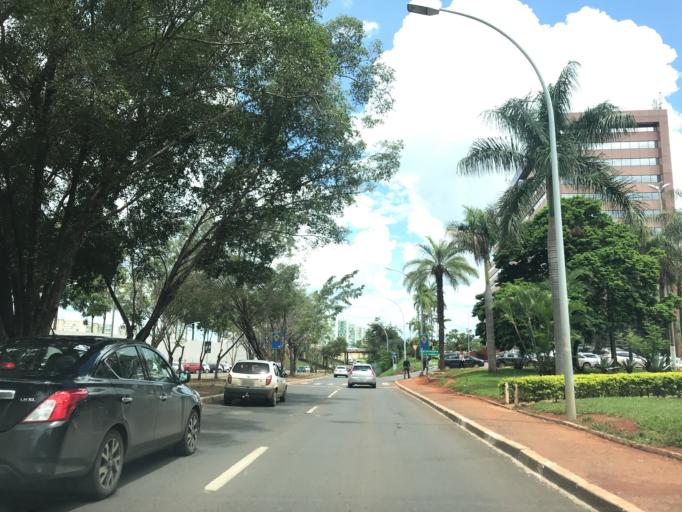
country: BR
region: Federal District
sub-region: Brasilia
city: Brasilia
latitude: -15.7982
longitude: -47.8793
